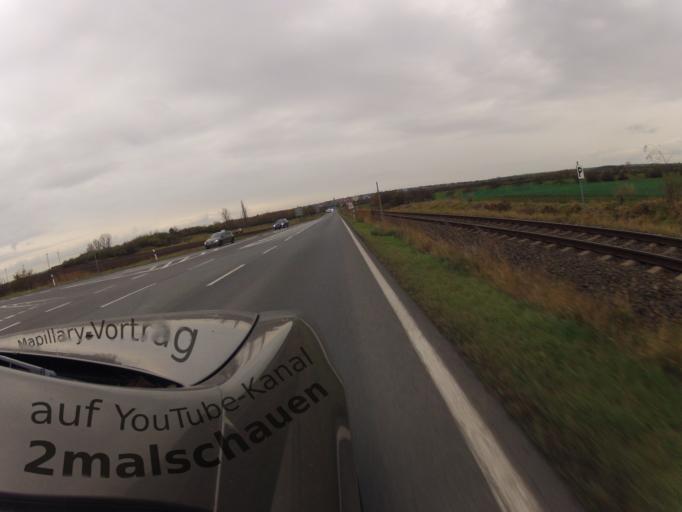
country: DE
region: Saxony-Anhalt
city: Konnern
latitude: 51.6895
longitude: 11.7668
